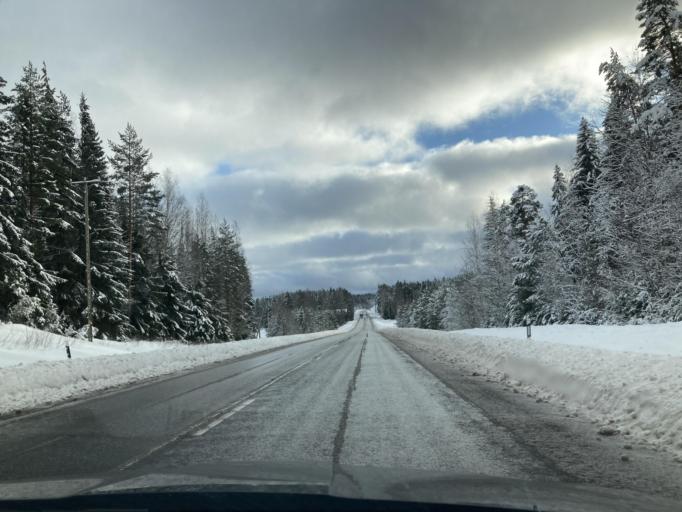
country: FI
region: Central Finland
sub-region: Jaemsae
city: Jaemsae
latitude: 61.7859
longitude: 25.2205
